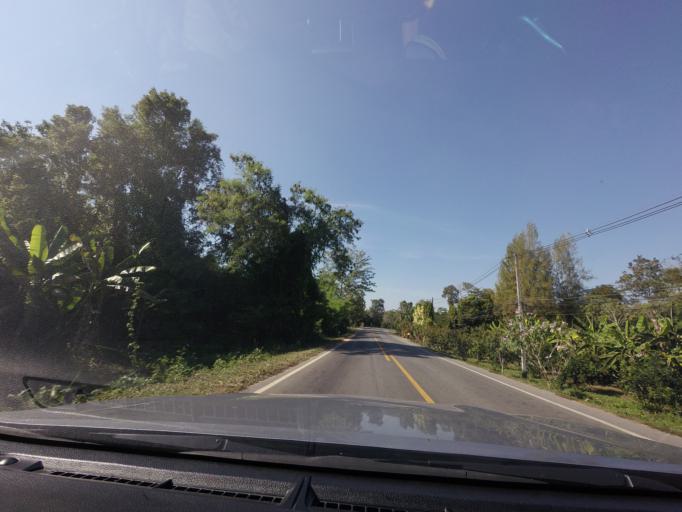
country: TH
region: Sukhothai
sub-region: Amphoe Si Satchanalai
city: Si Satchanalai
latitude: 17.6237
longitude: 99.7027
